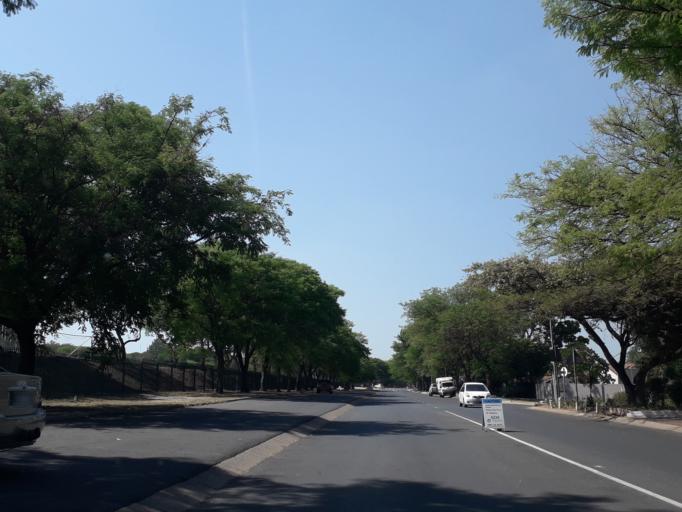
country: ZA
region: Gauteng
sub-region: City of Johannesburg Metropolitan Municipality
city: Diepsloot
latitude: -26.0260
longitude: 28.0036
